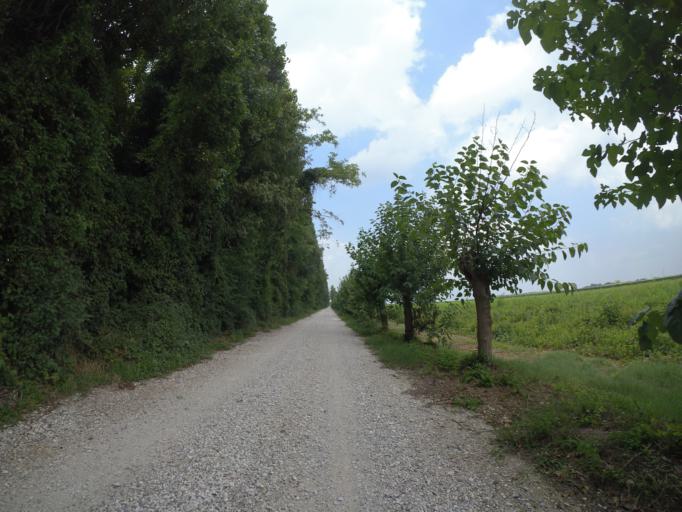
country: IT
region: Friuli Venezia Giulia
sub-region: Provincia di Udine
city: Sedegliano
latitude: 46.0027
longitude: 13.0107
